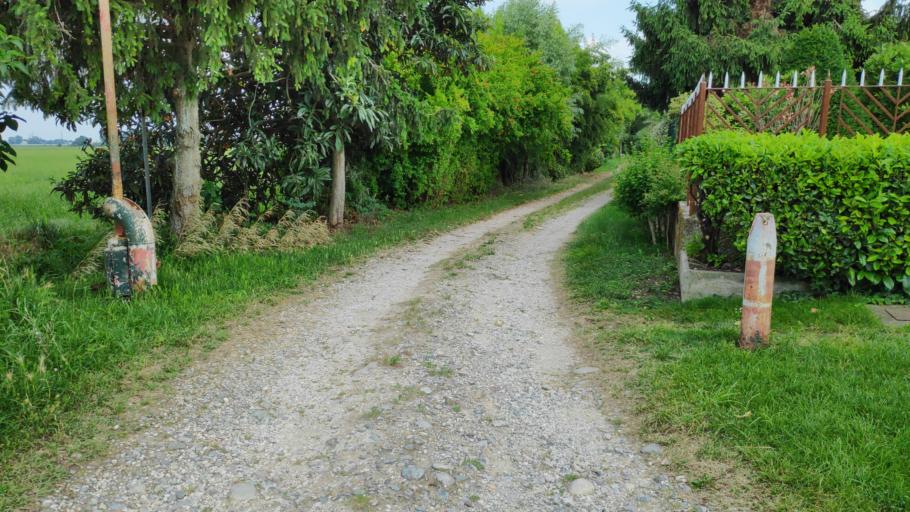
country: IT
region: Lombardy
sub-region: Citta metropolitana di Milano
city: Melzo
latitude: 45.4920
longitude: 9.4251
